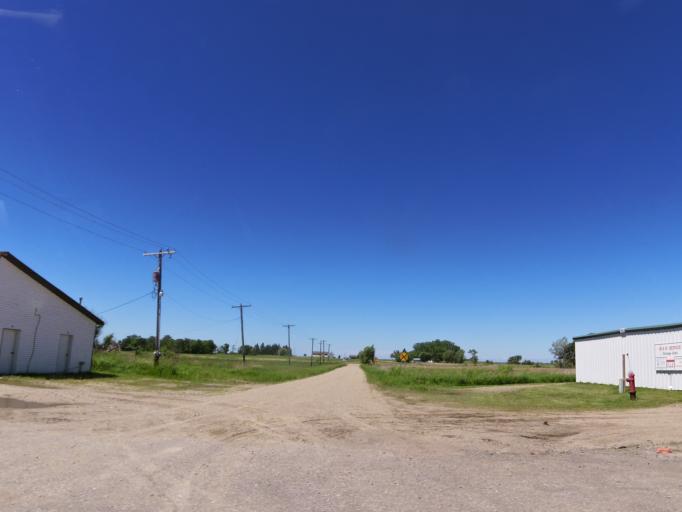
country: US
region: Minnesota
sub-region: Mahnomen County
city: Mahnomen
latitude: 47.1029
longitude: -95.9272
